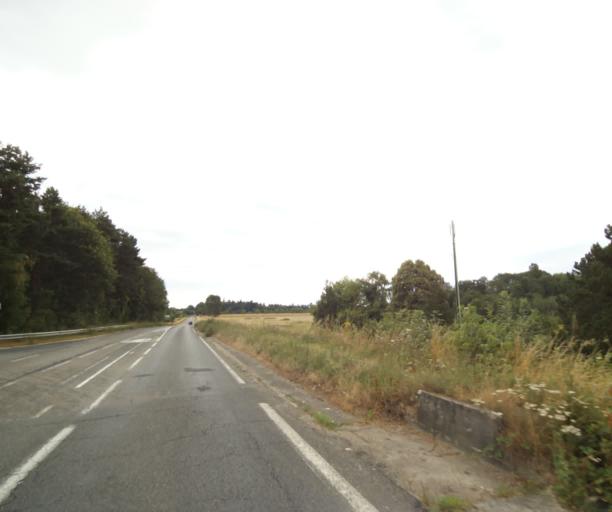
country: FR
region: Ile-de-France
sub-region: Departement de Seine-et-Marne
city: Cely
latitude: 48.4677
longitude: 2.5405
